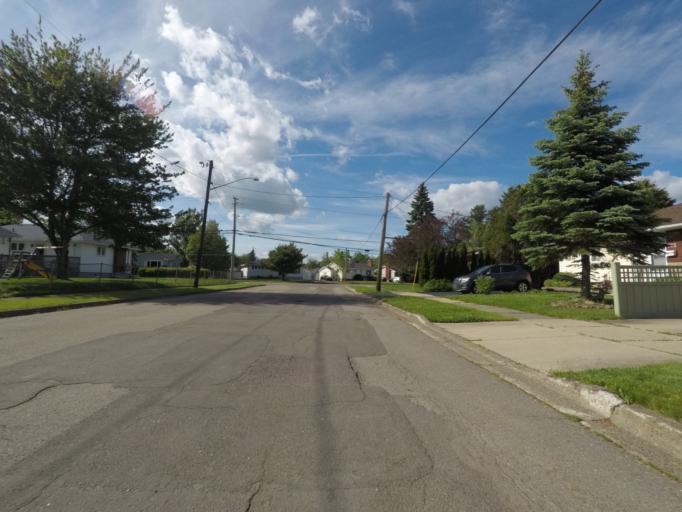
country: CA
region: New Brunswick
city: Moncton
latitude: 46.1031
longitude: -64.8265
